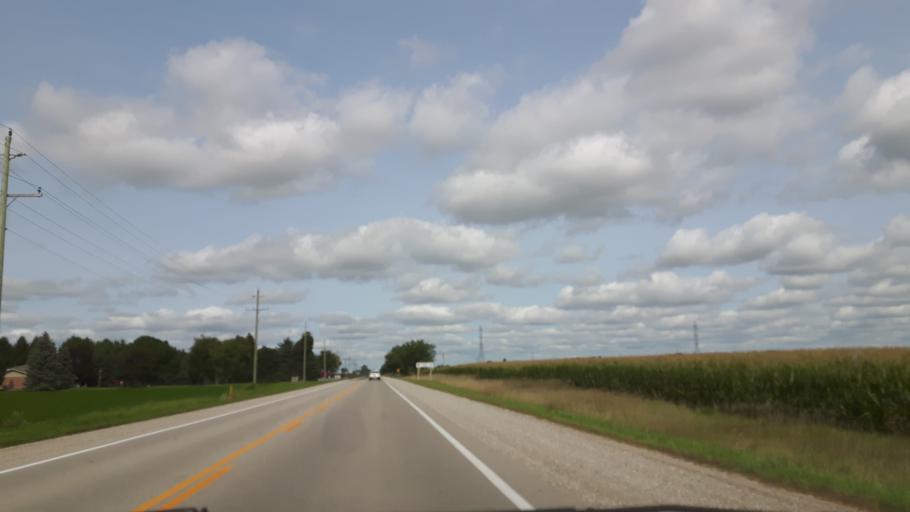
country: CA
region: Ontario
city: Huron East
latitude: 43.5655
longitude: -81.3831
